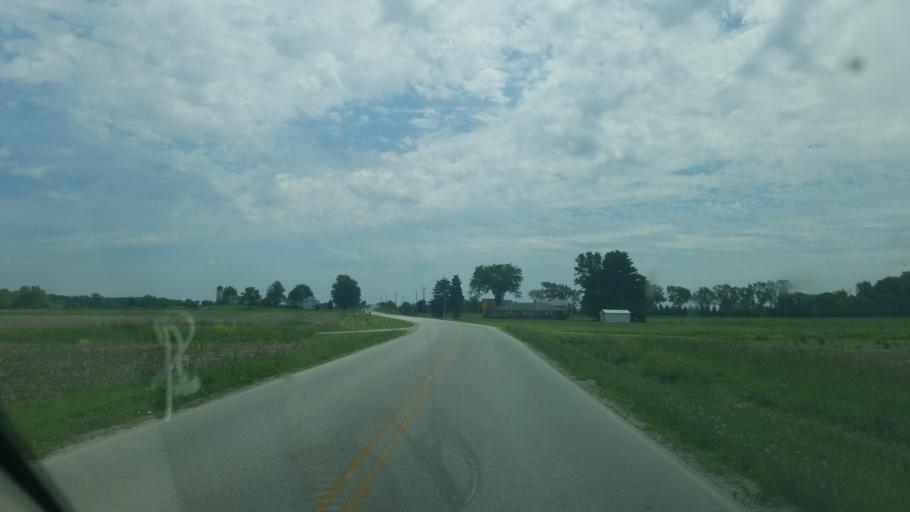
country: US
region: Ohio
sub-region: Wood County
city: Bowling Green
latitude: 41.2970
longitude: -83.6414
